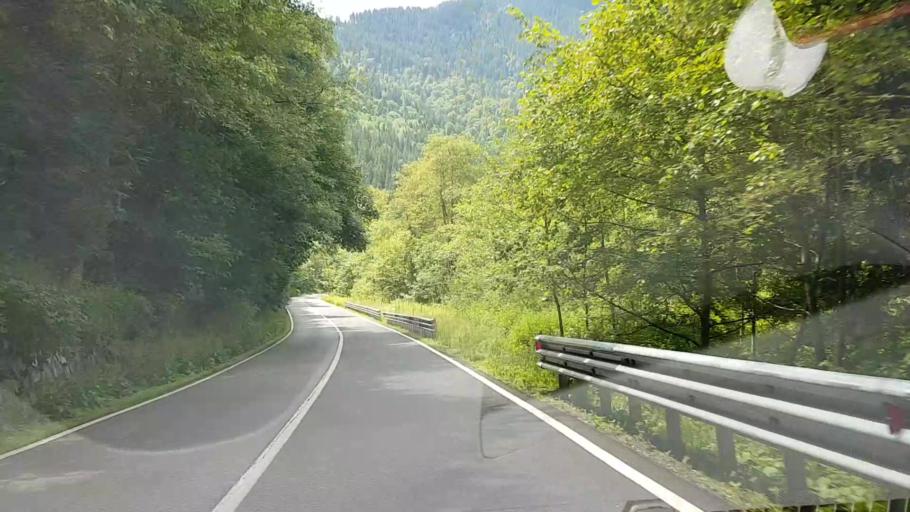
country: RO
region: Suceava
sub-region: Comuna Crucea
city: Crucea
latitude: 47.3849
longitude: 25.5784
